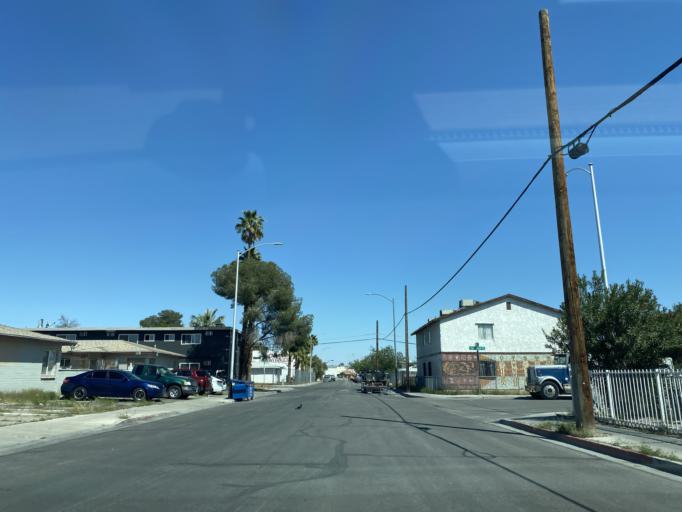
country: US
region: Nevada
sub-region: Clark County
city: Las Vegas
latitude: 36.1507
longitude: -115.1582
